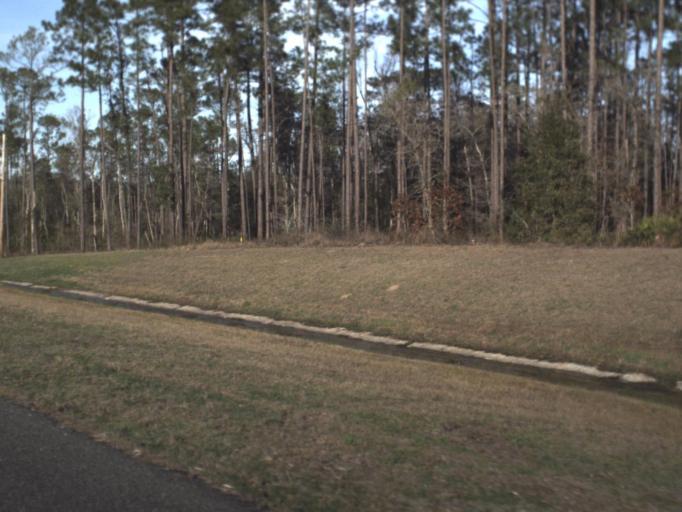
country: US
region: Florida
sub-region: Bay County
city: Laguna Beach
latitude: 30.4077
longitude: -85.8699
